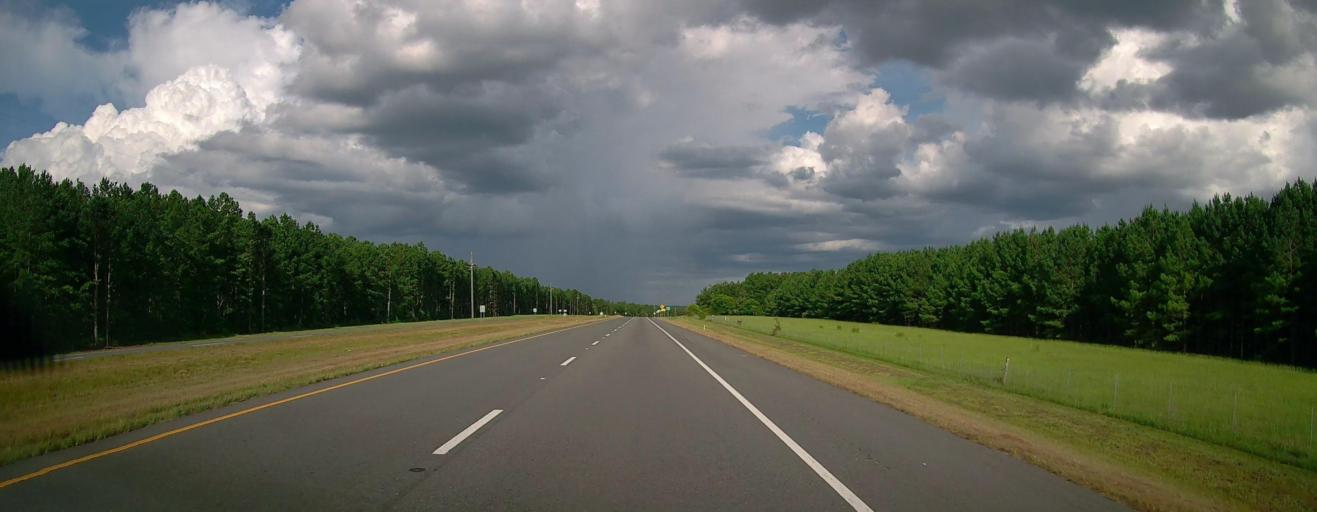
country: US
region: Georgia
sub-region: Talbot County
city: Talbotton
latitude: 32.5944
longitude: -84.4114
